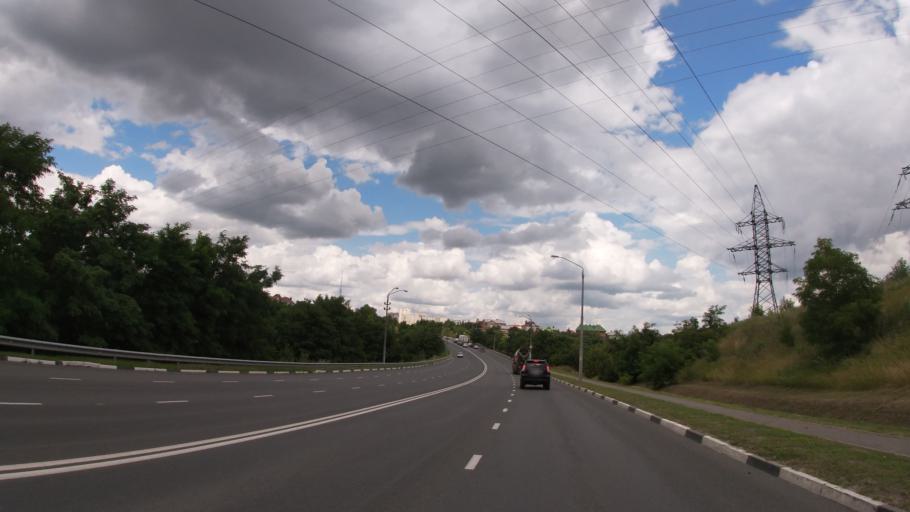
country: RU
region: Belgorod
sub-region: Belgorodskiy Rayon
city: Belgorod
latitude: 50.5581
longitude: 36.5861
